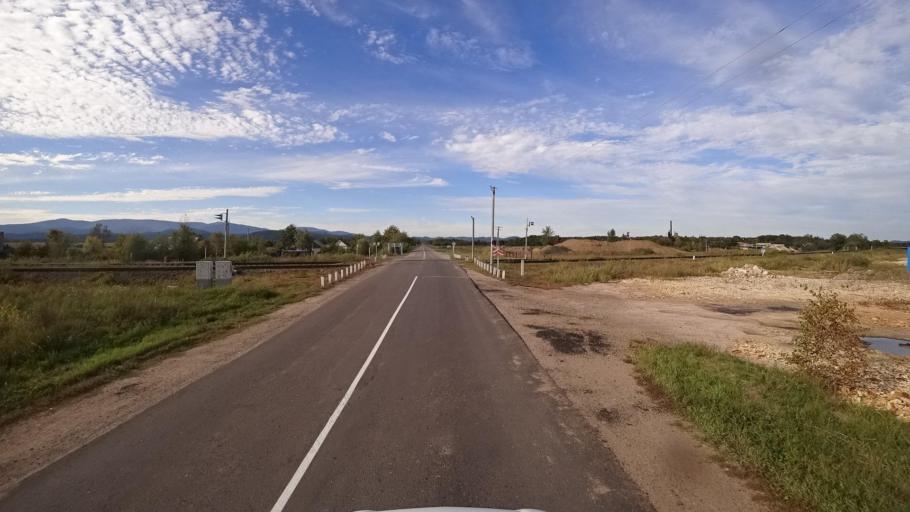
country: RU
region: Primorskiy
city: Dostoyevka
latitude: 44.2961
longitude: 133.4265
